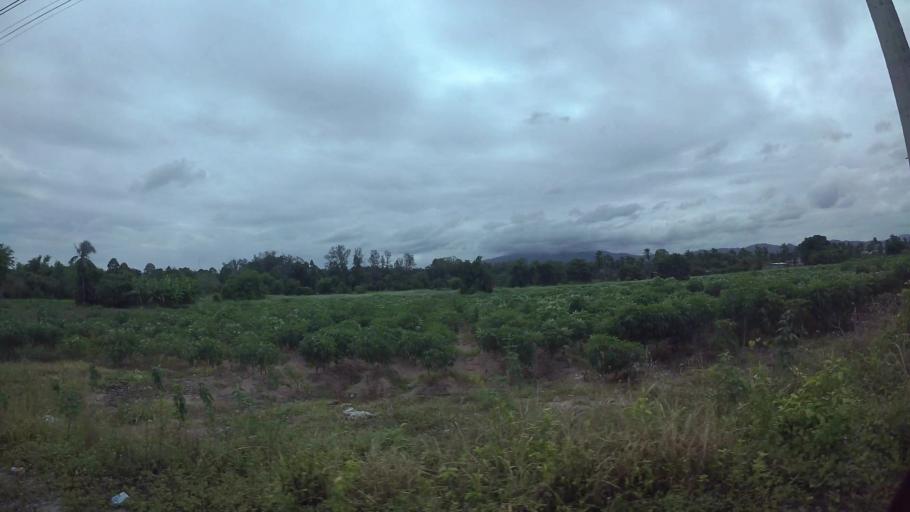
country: TH
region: Chon Buri
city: Si Racha
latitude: 13.1832
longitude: 100.9916
